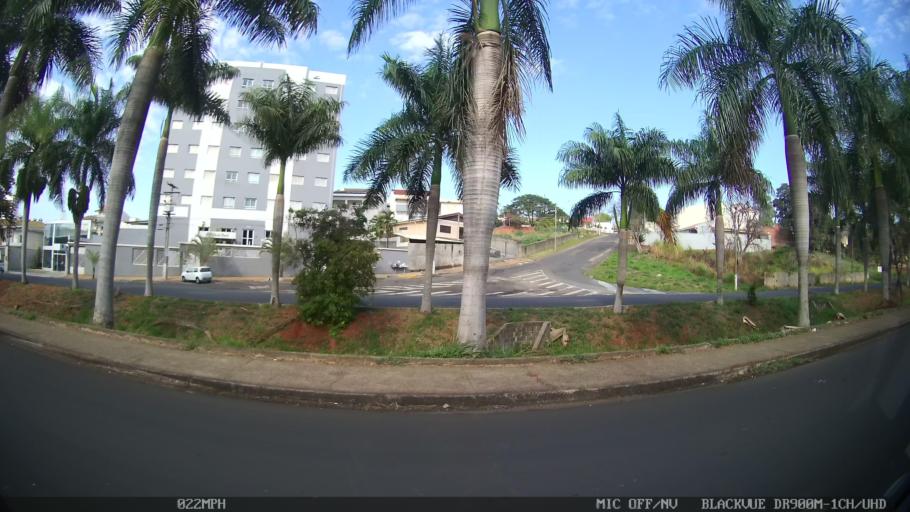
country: BR
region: Sao Paulo
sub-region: Americana
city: Americana
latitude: -22.7354
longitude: -47.3396
